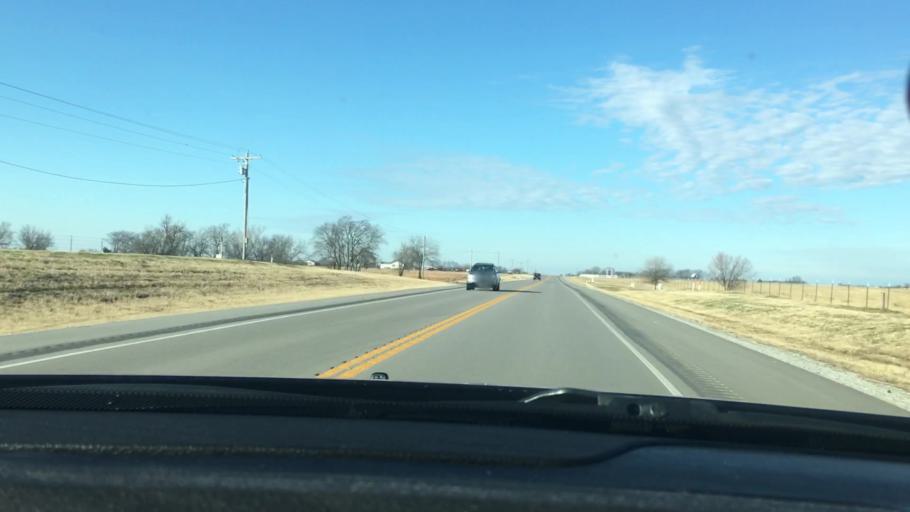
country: US
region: Oklahoma
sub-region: Love County
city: Marietta
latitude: 33.9404
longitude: -97.1875
